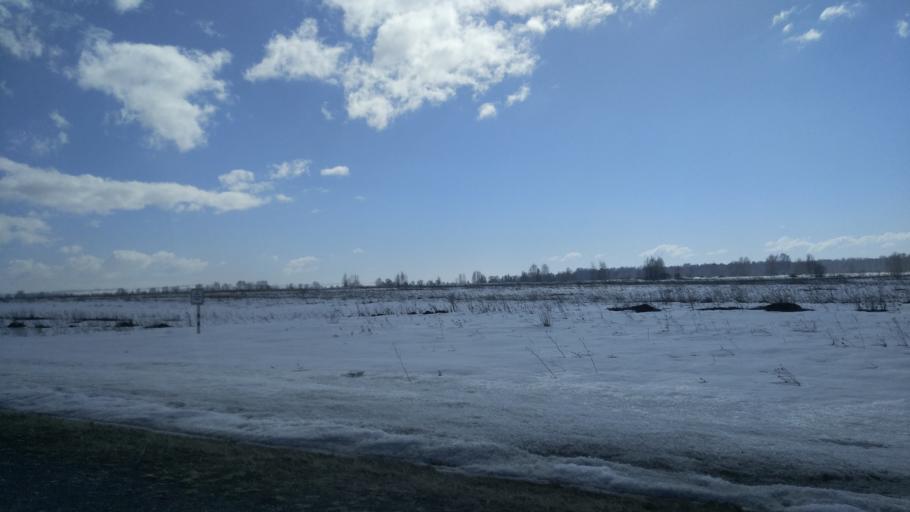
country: RU
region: Kemerovo
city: Yurga
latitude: 55.6838
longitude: 85.0234
